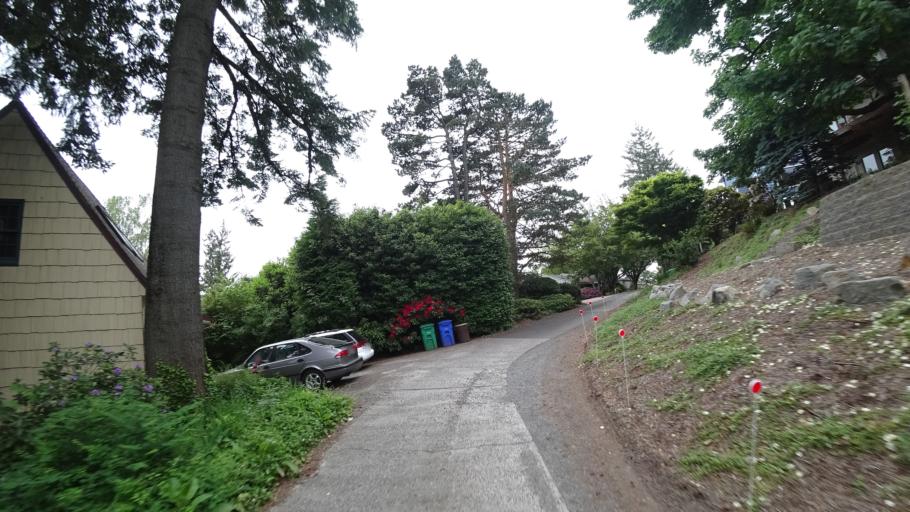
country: US
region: Oregon
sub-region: Multnomah County
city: Portland
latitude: 45.4841
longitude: -122.6895
